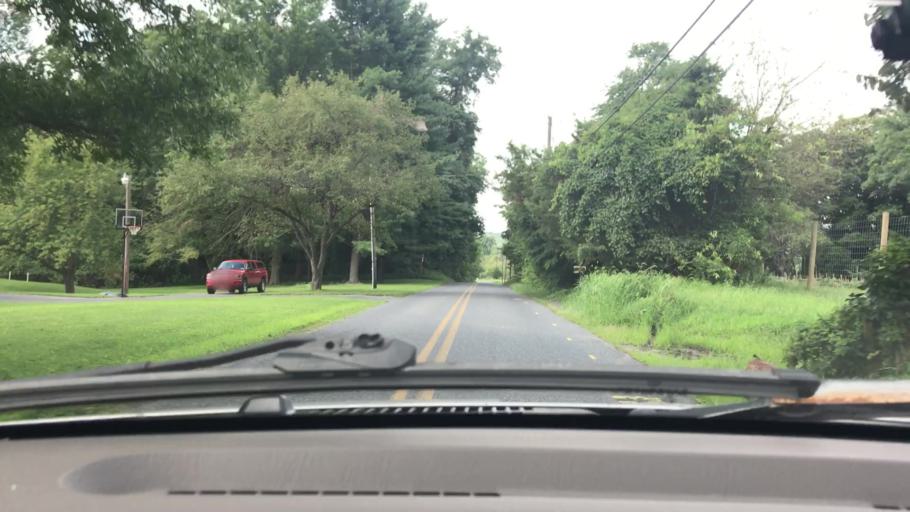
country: US
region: Pennsylvania
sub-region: Lancaster County
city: Elizabethtown
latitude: 40.1690
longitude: -76.6193
